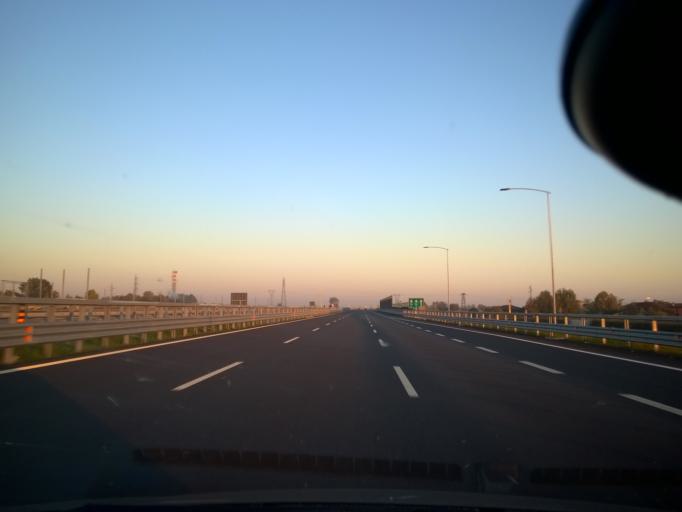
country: IT
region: Lombardy
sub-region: Provincia di Bergamo
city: Casirate d'Adda
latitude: 45.5071
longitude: 9.5600
